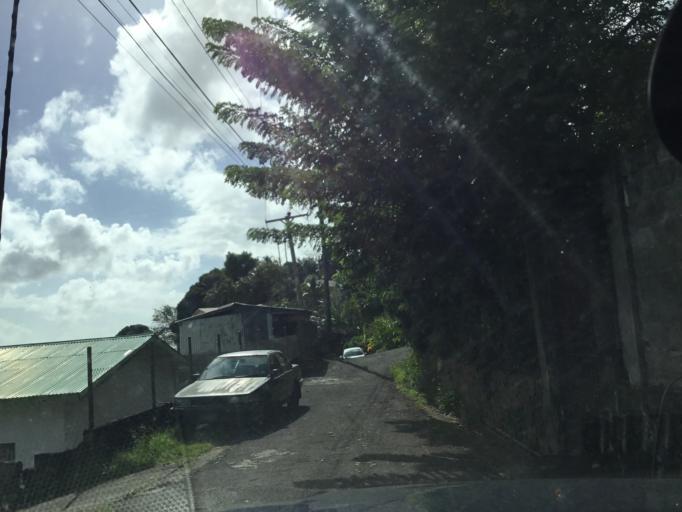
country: VC
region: Saint George
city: Kingstown
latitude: 13.1652
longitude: -61.2173
